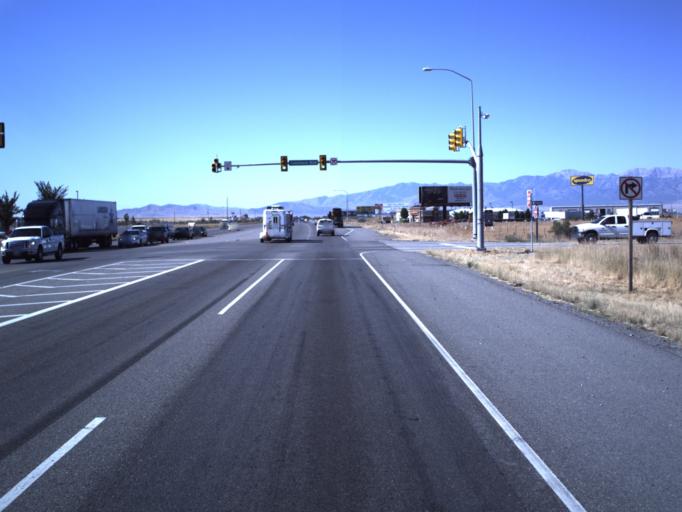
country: US
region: Utah
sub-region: Tooele County
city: Stansbury park
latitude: 40.6863
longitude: -112.2682
